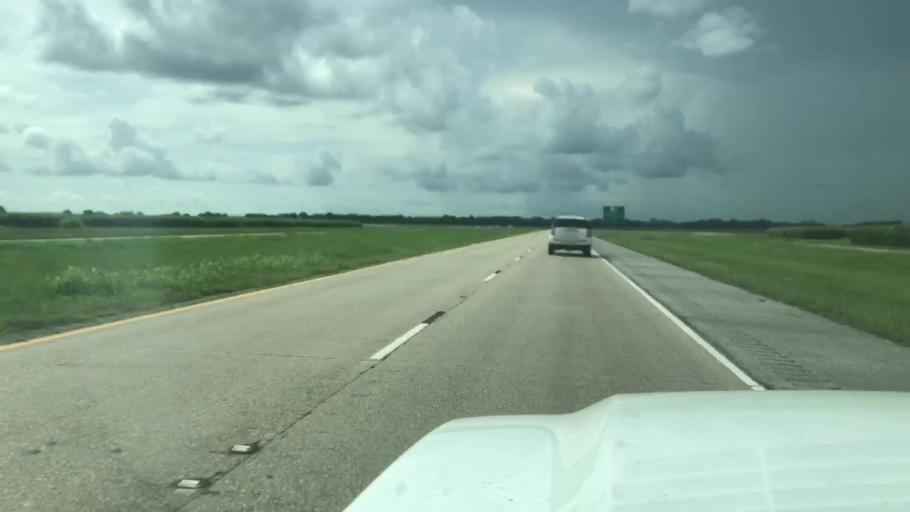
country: US
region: Louisiana
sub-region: Saint Mary Parish
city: Franklin
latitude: 29.7546
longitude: -91.4523
